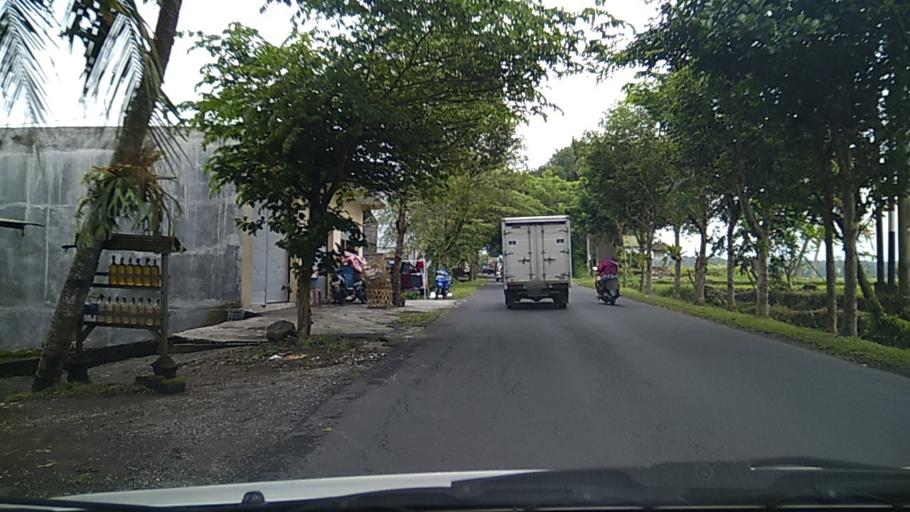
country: ID
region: Bali
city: Banjar Kembangsari
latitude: -8.4992
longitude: 115.2100
